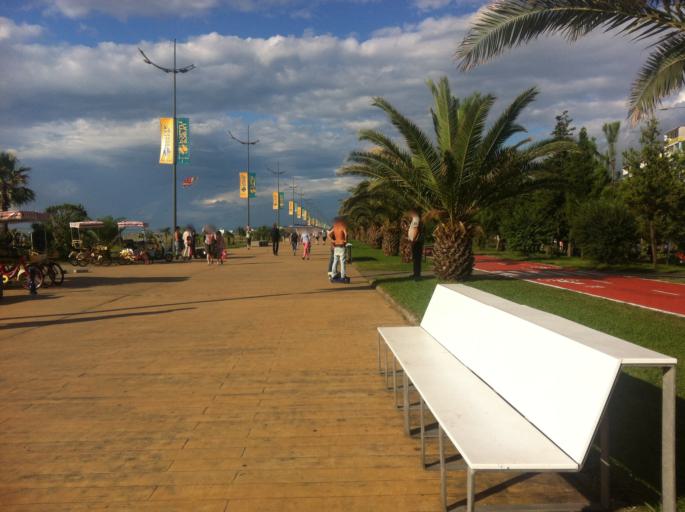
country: GE
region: Ajaria
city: Batumi
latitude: 41.6457
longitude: 41.6177
